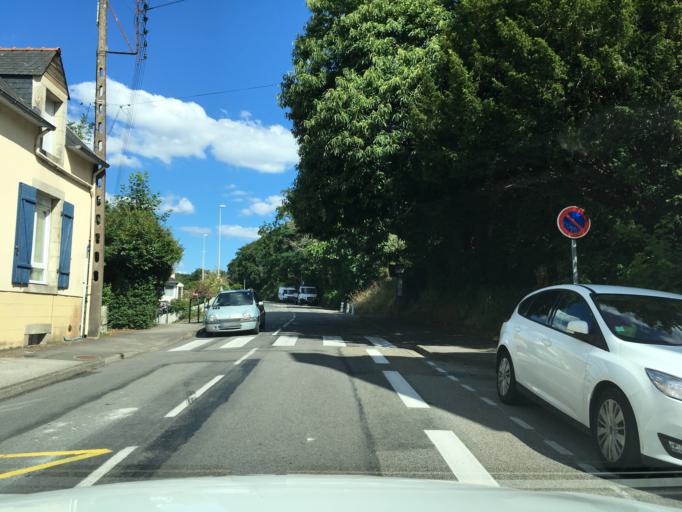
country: FR
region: Brittany
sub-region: Departement du Finistere
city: Quimper
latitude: 47.9884
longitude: -4.0791
